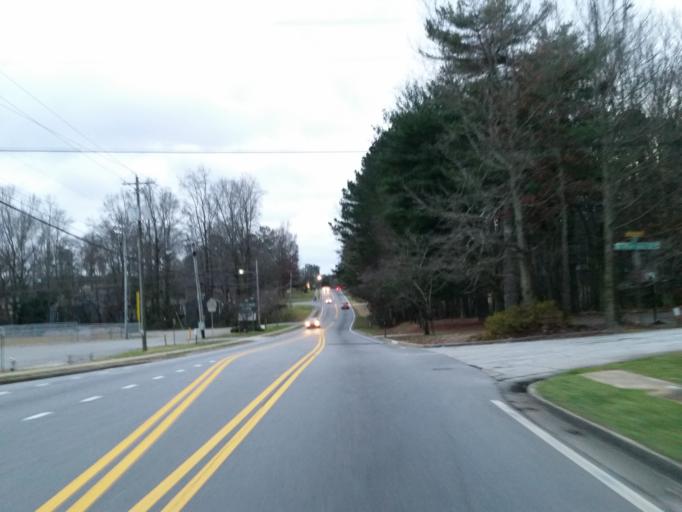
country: US
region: Georgia
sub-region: Cobb County
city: Fair Oaks
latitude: 33.8803
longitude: -84.5798
